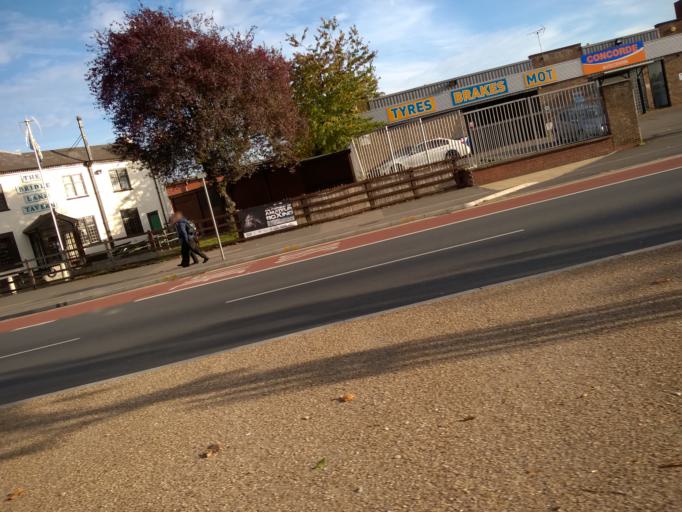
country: GB
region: England
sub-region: City of Leicester
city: Leicester
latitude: 52.6438
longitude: -1.1273
